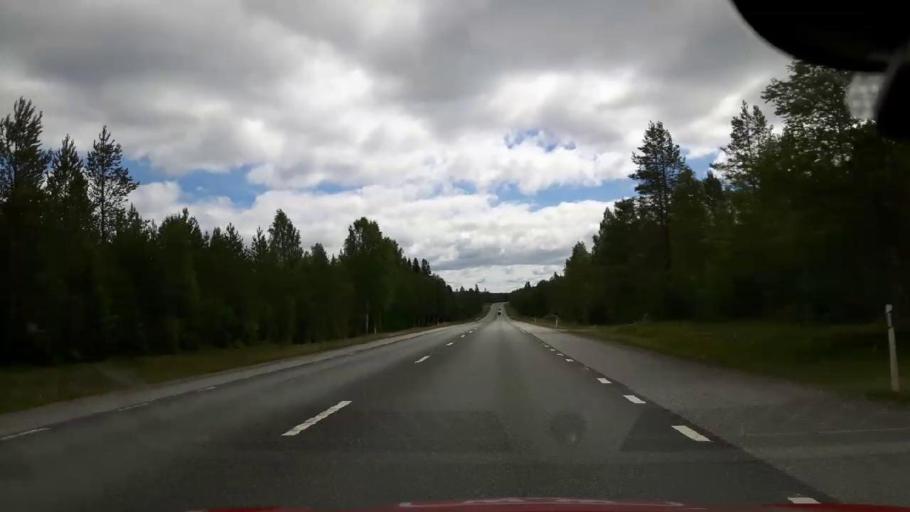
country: SE
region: Jaemtland
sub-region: Braecke Kommun
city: Braecke
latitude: 62.6889
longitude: 15.5583
